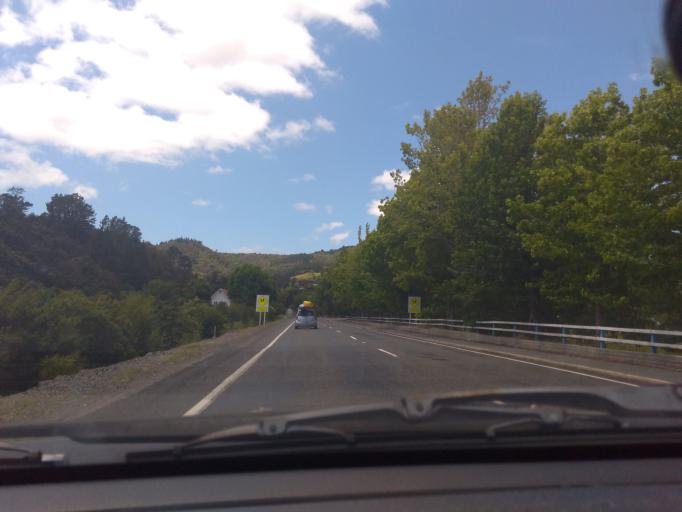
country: NZ
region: Northland
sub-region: Far North District
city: Kerikeri
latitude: -35.1007
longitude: 173.7834
